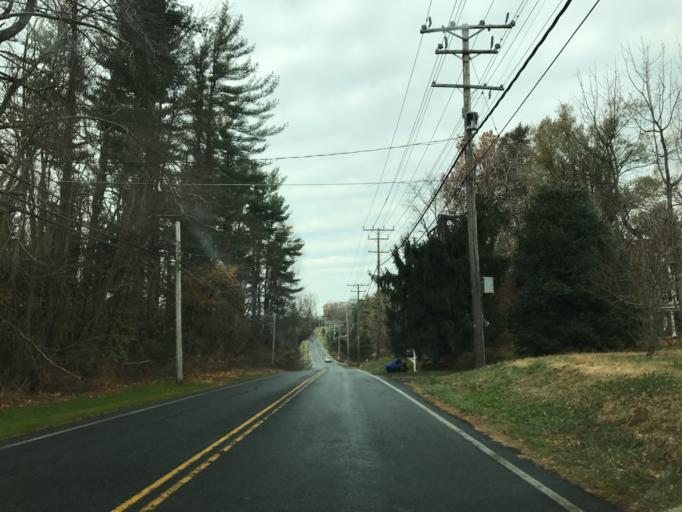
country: US
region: Maryland
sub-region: Harford County
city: Jarrettsville
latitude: 39.6054
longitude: -76.4439
